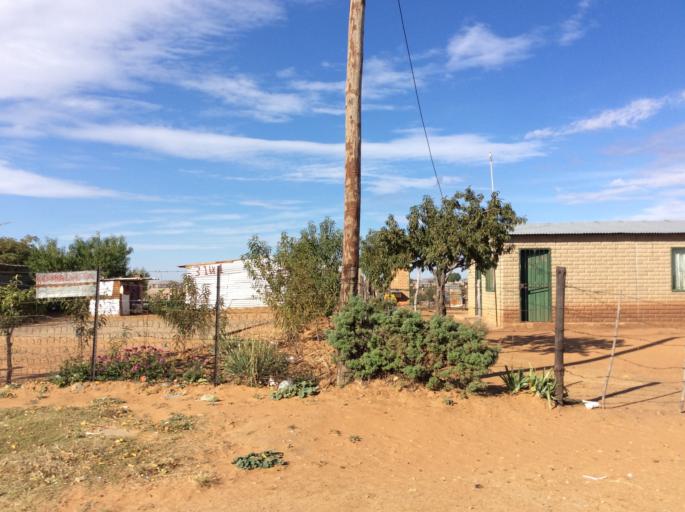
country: LS
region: Mafeteng
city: Mafeteng
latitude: -29.7164
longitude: 27.0133
